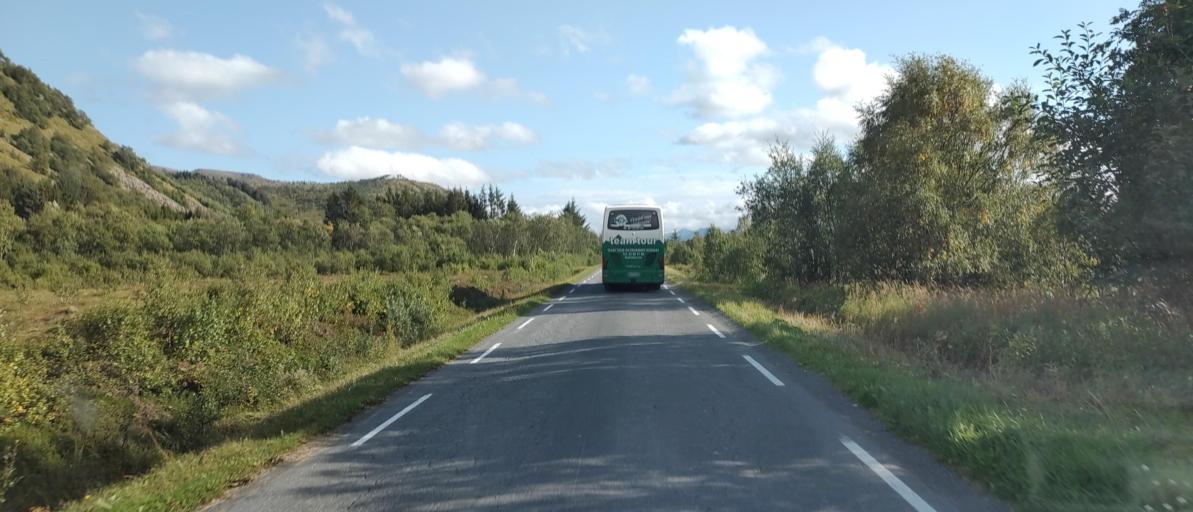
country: NO
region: Nordland
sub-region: Sortland
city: Sortland
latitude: 69.0342
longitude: 15.5264
